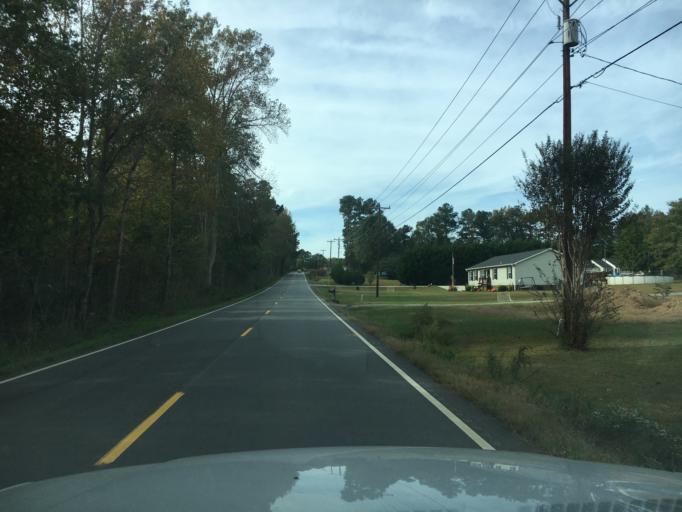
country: US
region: South Carolina
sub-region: Spartanburg County
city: Duncan
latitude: 34.8870
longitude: -82.1313
